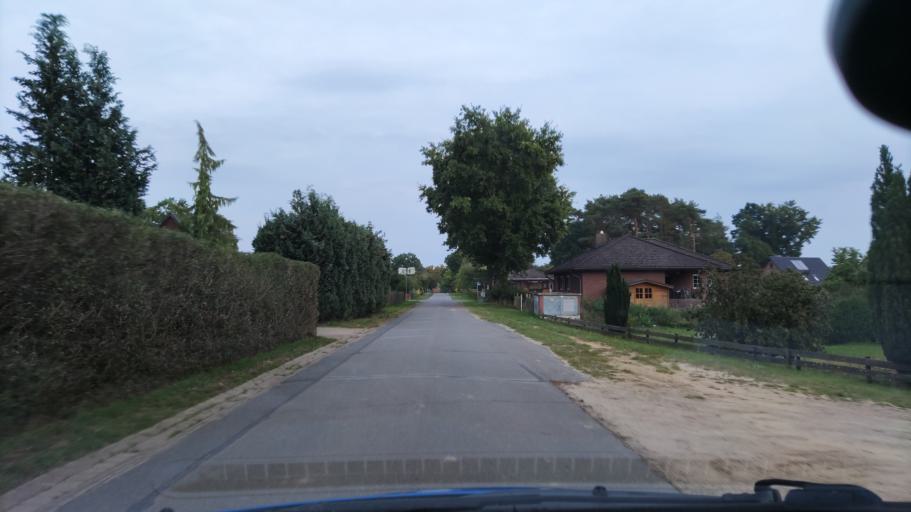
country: DE
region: Lower Saxony
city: Karwitz
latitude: 53.0897
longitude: 10.9980
